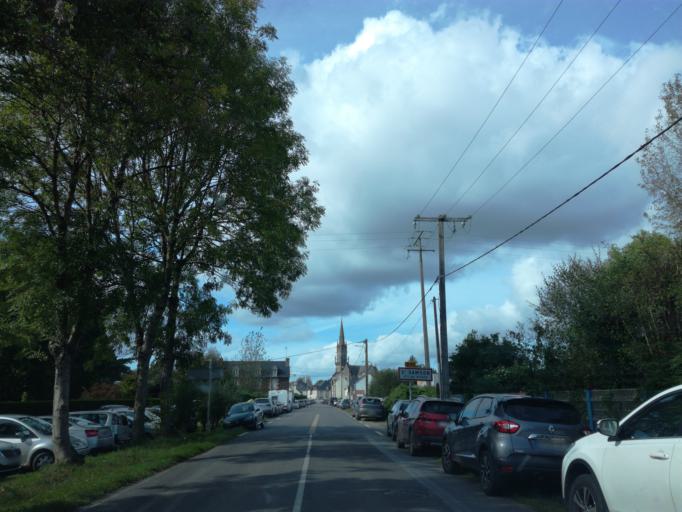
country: FR
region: Brittany
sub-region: Departement du Morbihan
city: Rohan
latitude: 48.0846
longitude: -2.7640
